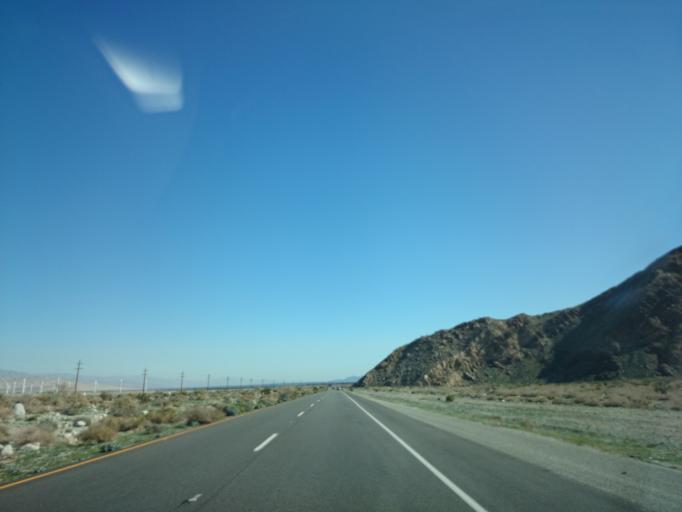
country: US
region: California
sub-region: Riverside County
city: Garnet
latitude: 33.8827
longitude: -116.5959
